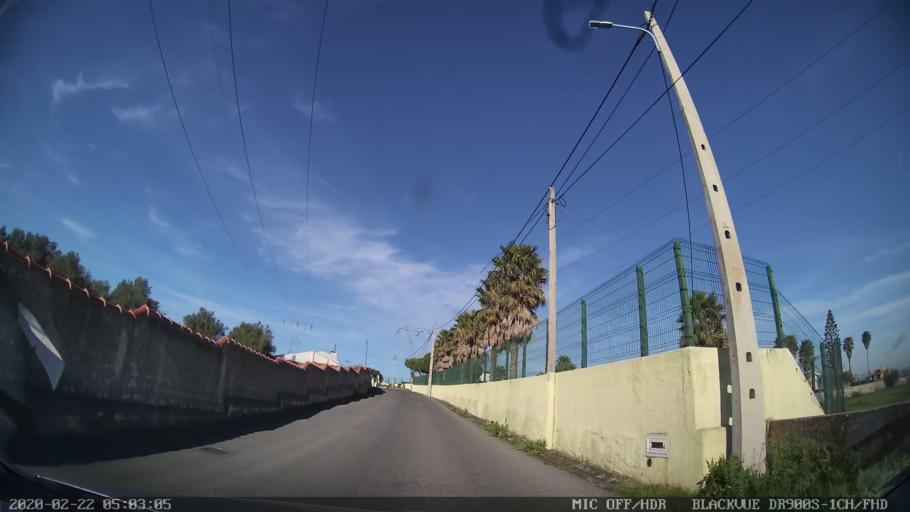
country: PT
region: Lisbon
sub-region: Vila Franca de Xira
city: Vila Franca de Xira
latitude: 38.9680
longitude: -8.9955
